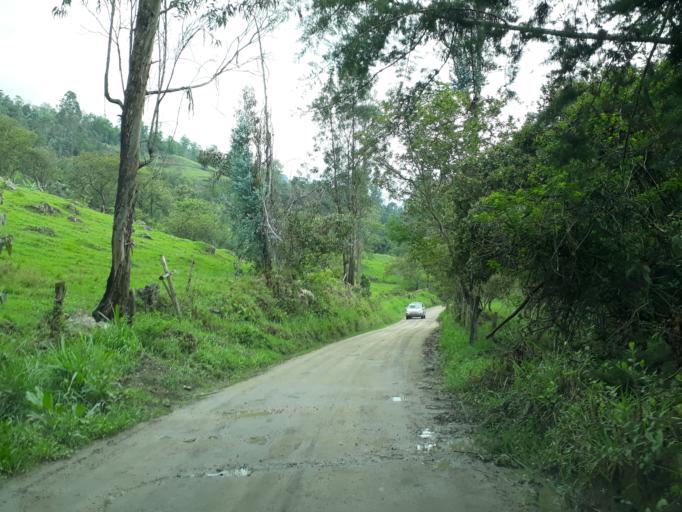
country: CO
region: Cundinamarca
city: Manta
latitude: 4.9994
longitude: -73.5514
